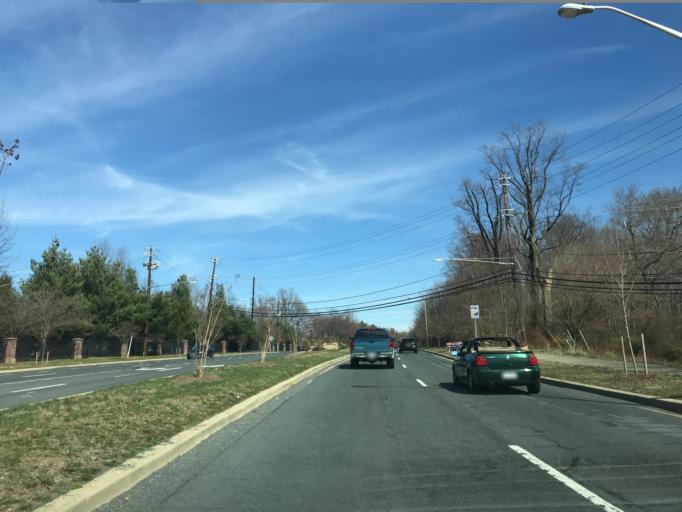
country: US
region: Maryland
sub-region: Prince George's County
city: Lake Arbor
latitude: 38.9165
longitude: -76.8319
